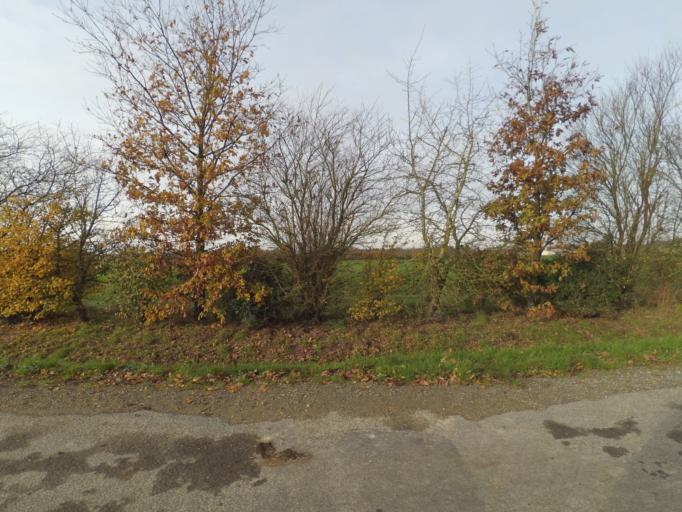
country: FR
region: Pays de la Loire
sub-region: Departement de la Loire-Atlantique
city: La Planche
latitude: 47.0174
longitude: -1.4079
